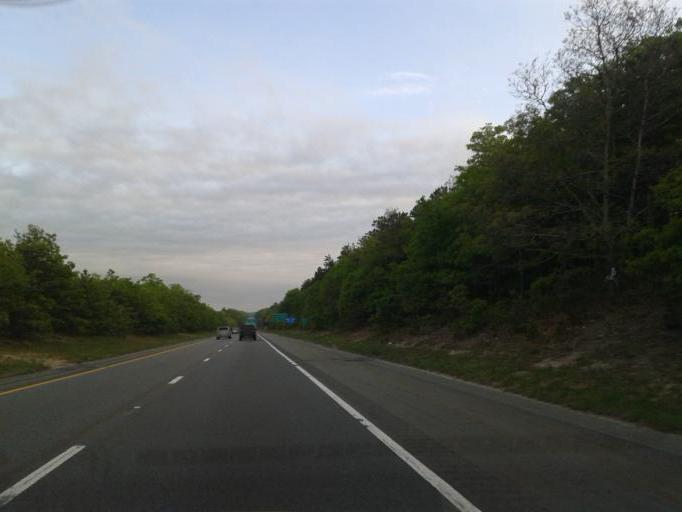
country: US
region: Massachusetts
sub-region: Barnstable County
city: North Falmouth
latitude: 41.6344
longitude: -70.6101
